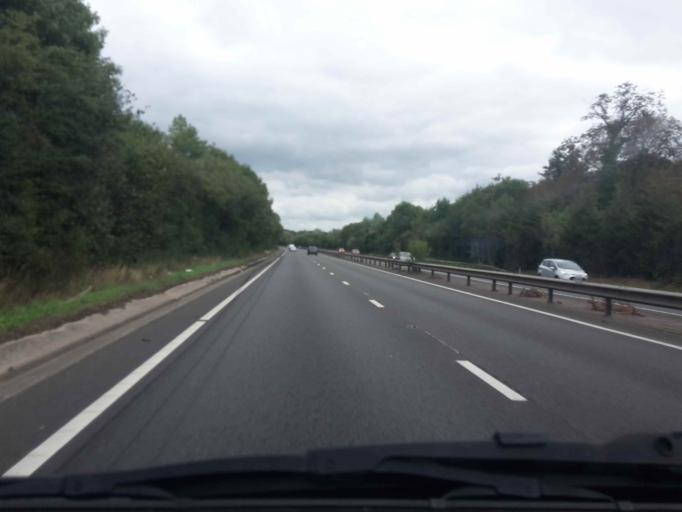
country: GB
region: England
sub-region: Surrey
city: Seale
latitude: 51.2485
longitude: -0.7324
